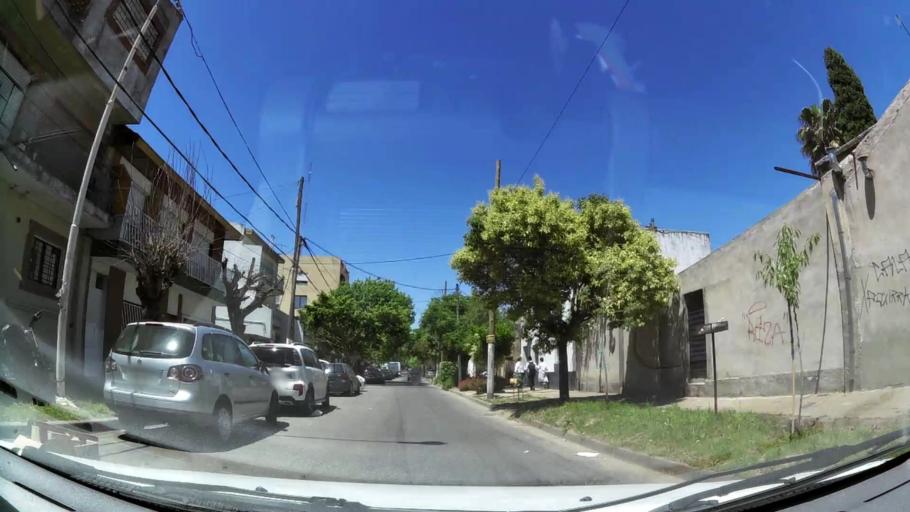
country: AR
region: Buenos Aires
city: Caseros
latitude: -34.6025
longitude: -58.5585
